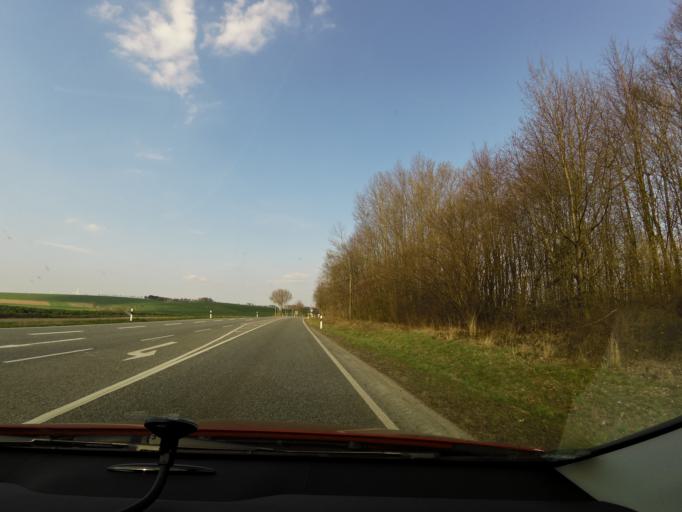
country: DE
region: Lower Saxony
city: Bodensee
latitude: 51.5836
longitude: 10.1420
